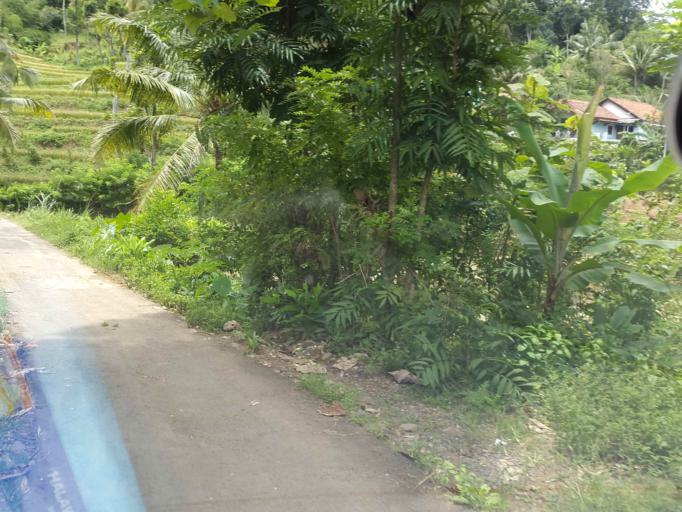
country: ID
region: Central Java
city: Muara
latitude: -7.2604
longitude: 108.8849
